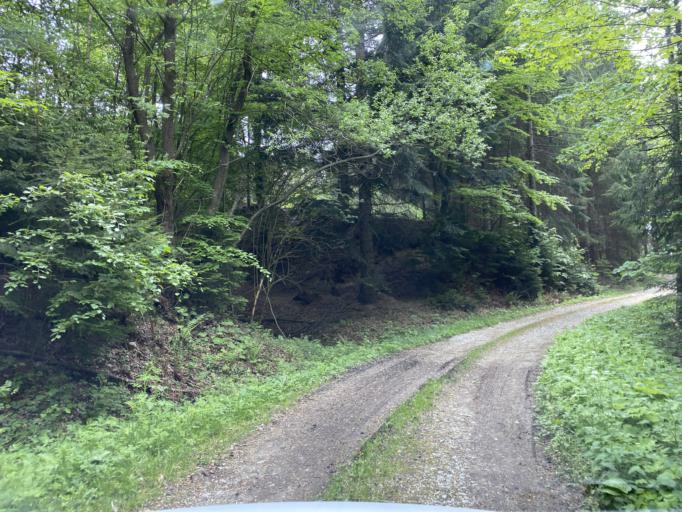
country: AT
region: Styria
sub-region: Politischer Bezirk Weiz
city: Koglhof
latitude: 47.3098
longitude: 15.7039
